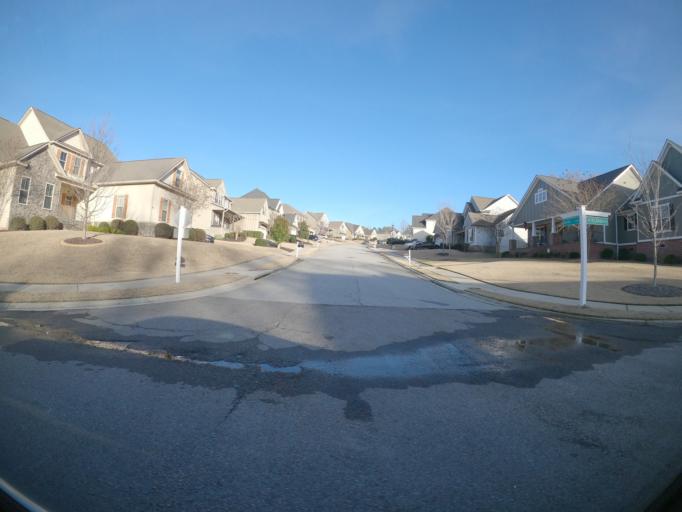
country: US
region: Georgia
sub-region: Columbia County
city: Evans
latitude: 33.5878
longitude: -82.2009
